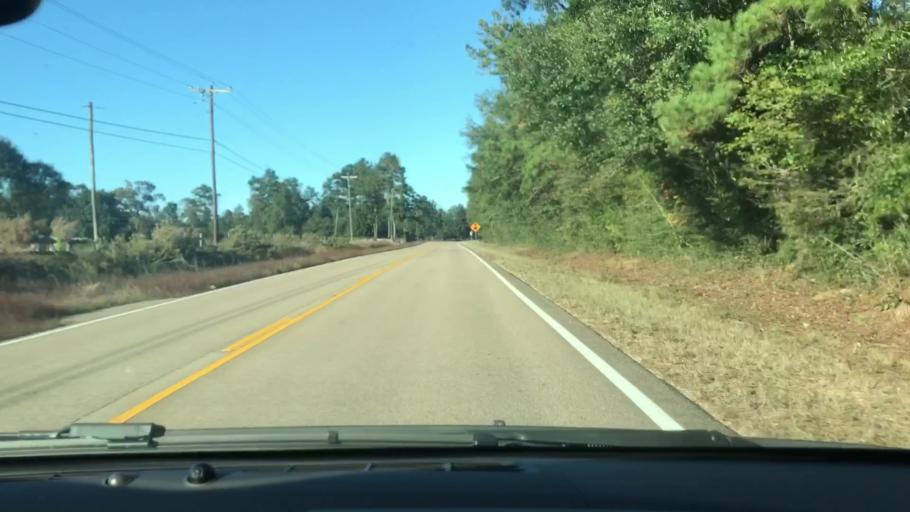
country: US
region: Louisiana
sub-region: Saint Tammany Parish
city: Abita Springs
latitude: 30.6349
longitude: -90.0158
